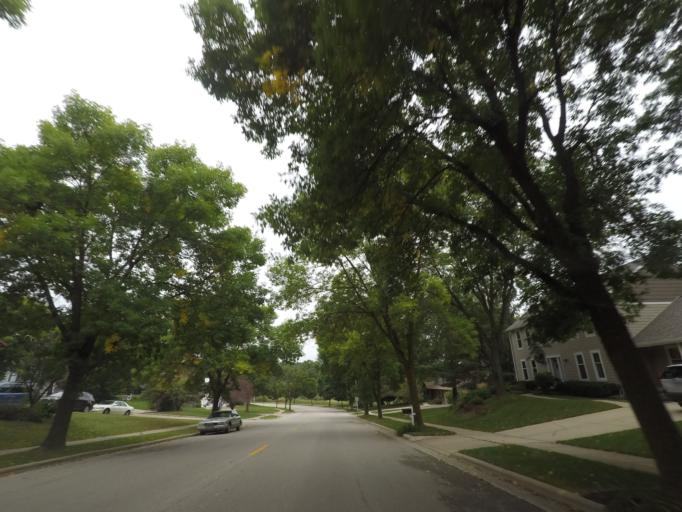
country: US
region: Wisconsin
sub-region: Dane County
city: Middleton
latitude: 43.0835
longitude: -89.5064
